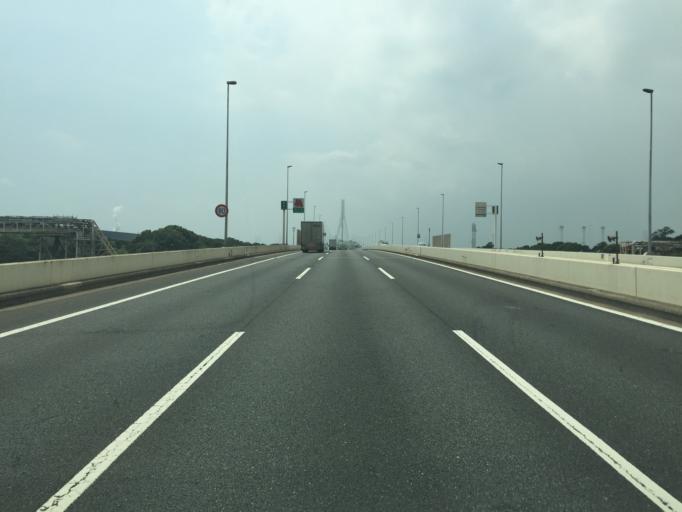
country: JP
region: Kanagawa
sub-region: Kawasaki-shi
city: Kawasaki
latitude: 35.4807
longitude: 139.7190
